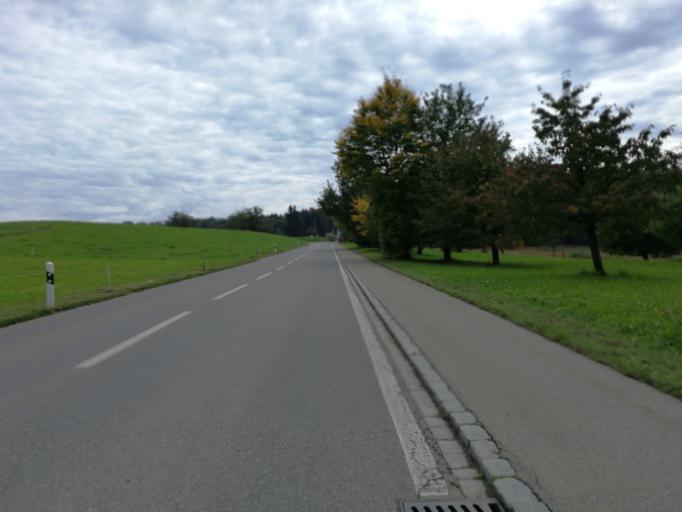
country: CH
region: Zurich
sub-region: Bezirk Meilen
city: Dorf
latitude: 47.2606
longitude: 8.7424
